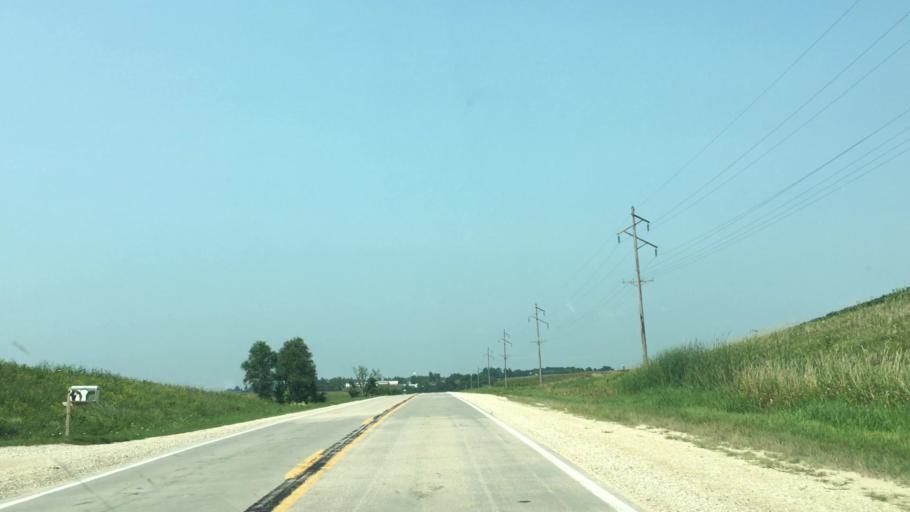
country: US
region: Iowa
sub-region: Winneshiek County
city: Decorah
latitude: 43.1490
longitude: -91.8643
